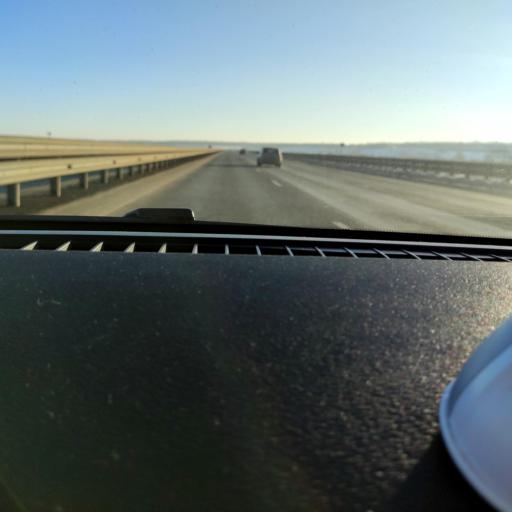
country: RU
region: Samara
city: Smyshlyayevka
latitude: 53.1545
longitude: 50.3478
